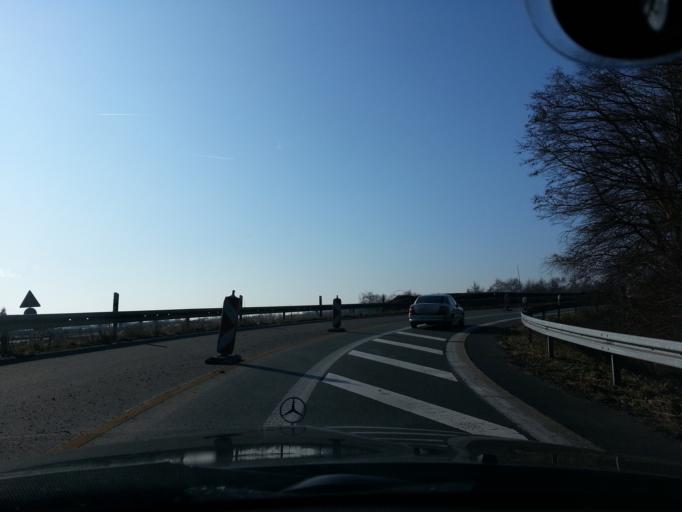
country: DE
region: North Rhine-Westphalia
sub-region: Regierungsbezirk Munster
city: Recklinghausen
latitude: 51.5828
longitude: 7.1912
